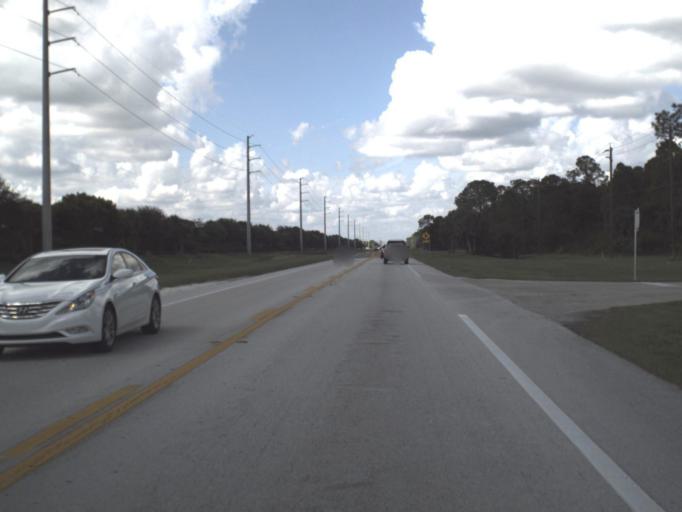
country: US
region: Florida
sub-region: Lee County
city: Gateway
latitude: 26.6015
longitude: -81.7481
